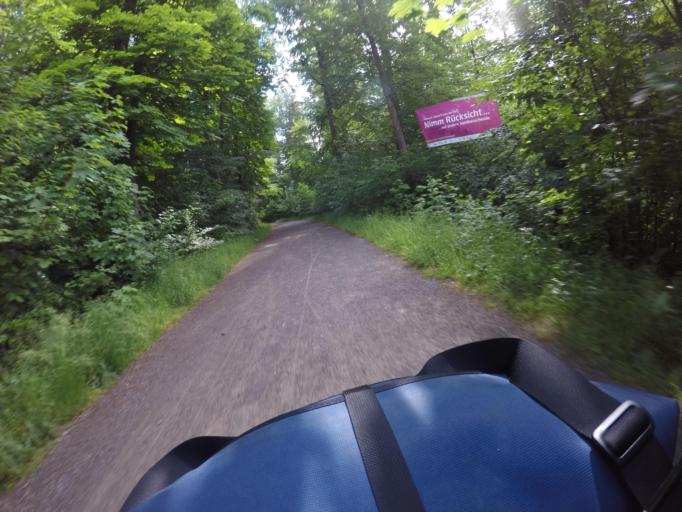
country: DE
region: Baden-Wuerttemberg
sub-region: Regierungsbezirk Stuttgart
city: Gerlingen
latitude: 48.7562
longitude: 9.0927
